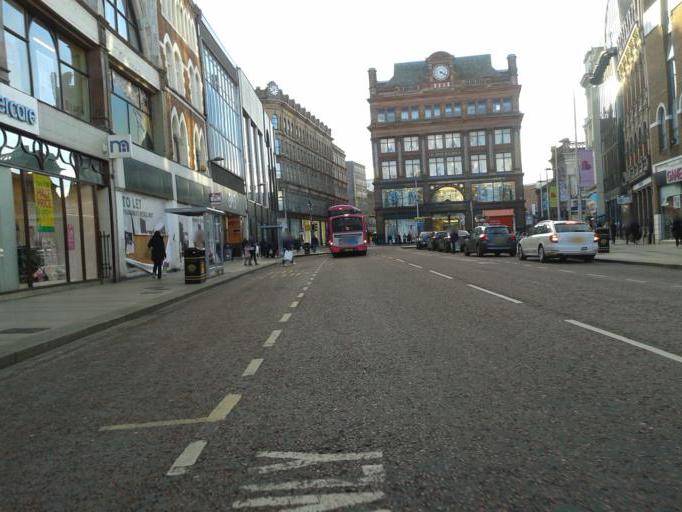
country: GB
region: Northern Ireland
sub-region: City of Belfast
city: Belfast
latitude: 54.5993
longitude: -5.9290
